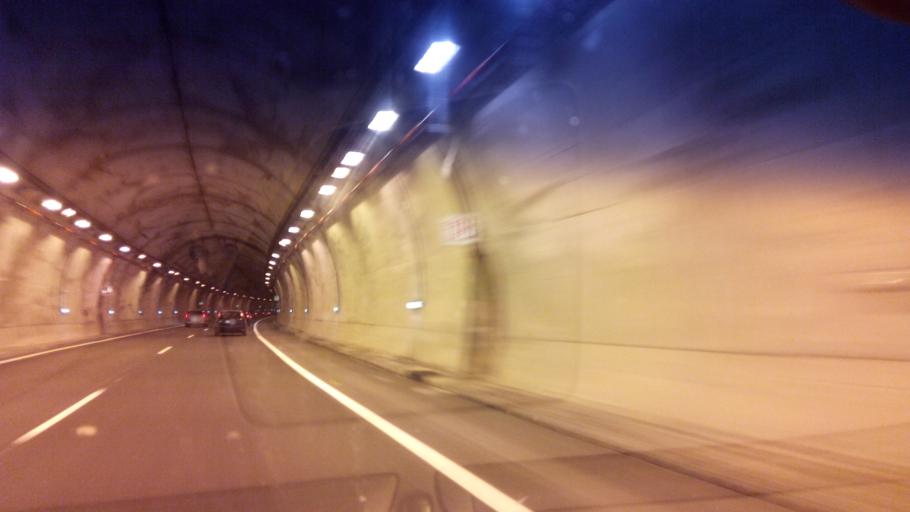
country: ES
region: Asturias
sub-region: Province of Asturias
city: Ribadesella
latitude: 43.4629
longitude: -5.1424
